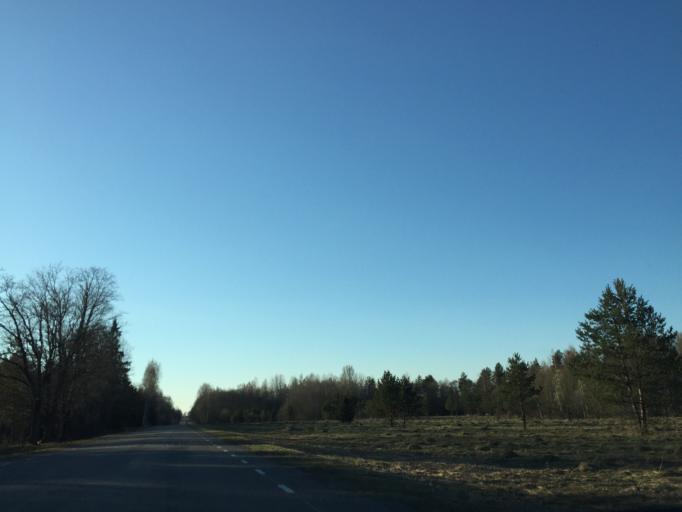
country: EE
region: Ida-Virumaa
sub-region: Sillamaee linn
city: Sillamae
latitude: 59.0865
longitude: 27.6688
